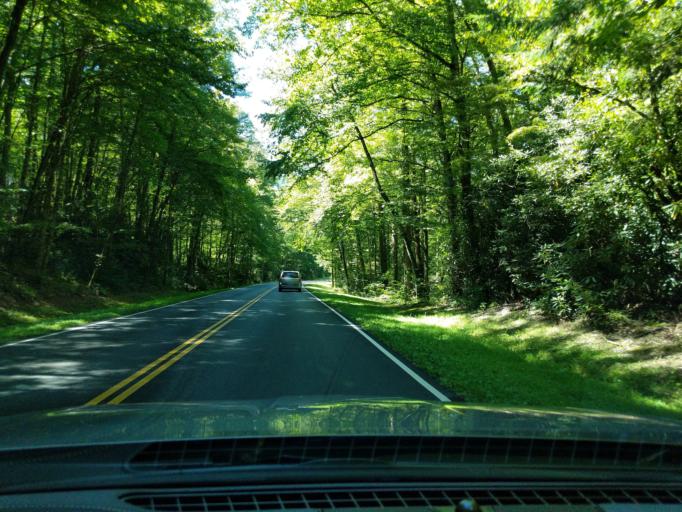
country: US
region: North Carolina
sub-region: Swain County
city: Cherokee
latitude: 35.5560
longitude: -83.3160
